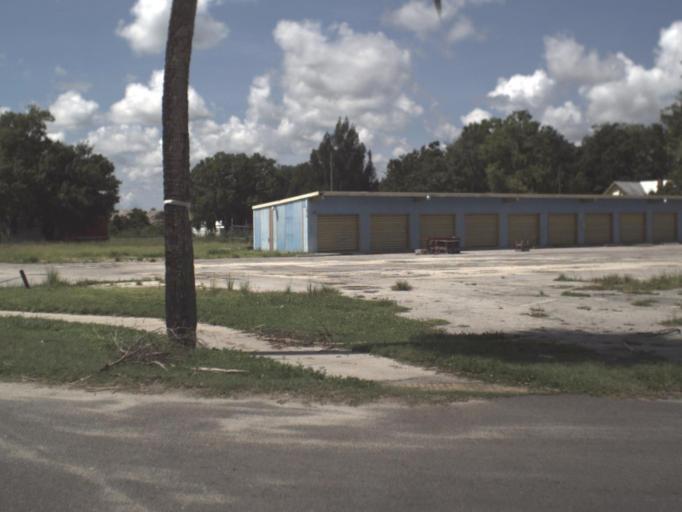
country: US
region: Florida
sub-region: DeSoto County
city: Arcadia
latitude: 27.2052
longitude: -81.8623
